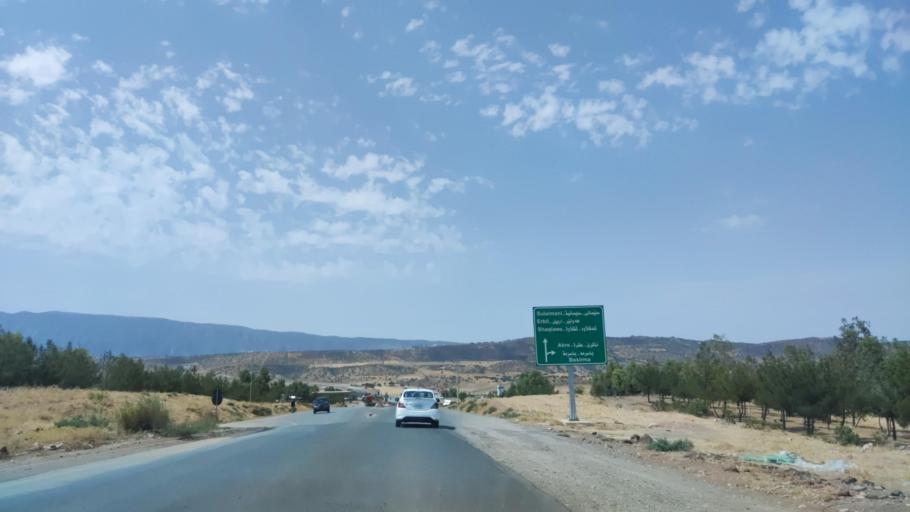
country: IQ
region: Arbil
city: Shaqlawah
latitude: 36.4594
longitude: 44.3880
